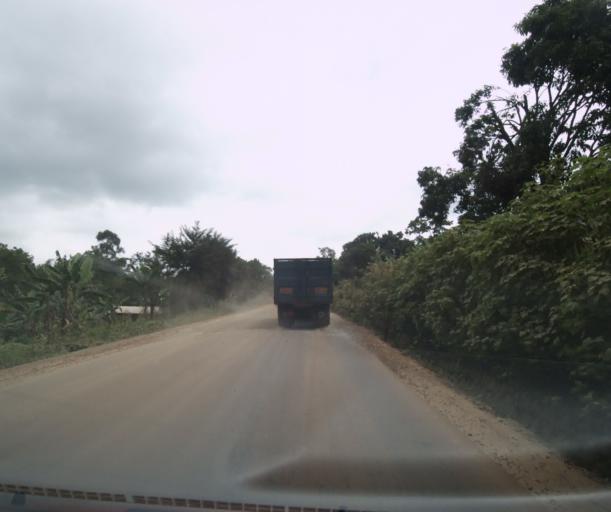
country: CM
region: West
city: Mbouda
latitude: 5.6666
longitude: 10.2194
